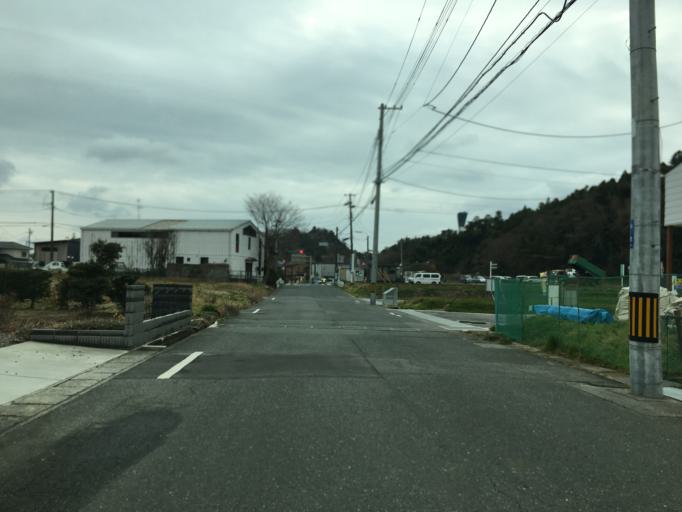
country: JP
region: Fukushima
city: Iwaki
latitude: 36.9460
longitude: 140.9241
